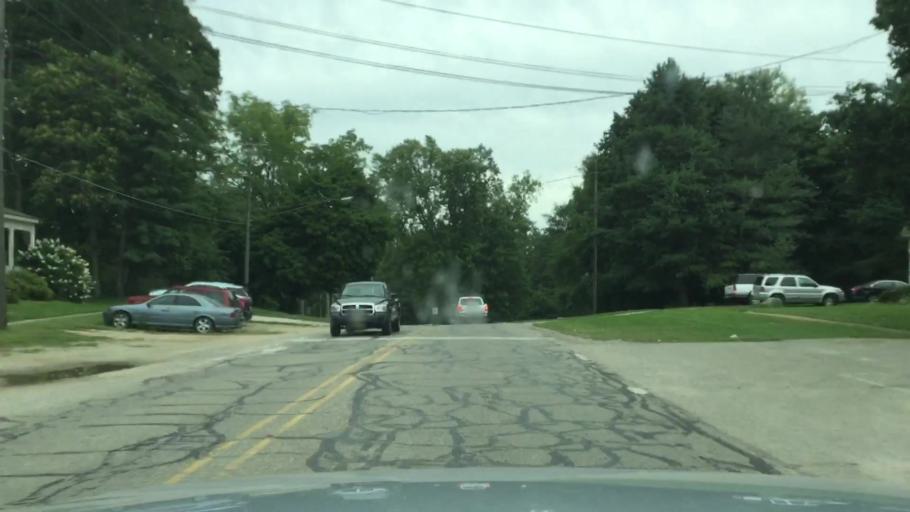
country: US
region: Michigan
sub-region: Shiawassee County
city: Durand
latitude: 42.8224
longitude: -83.9444
